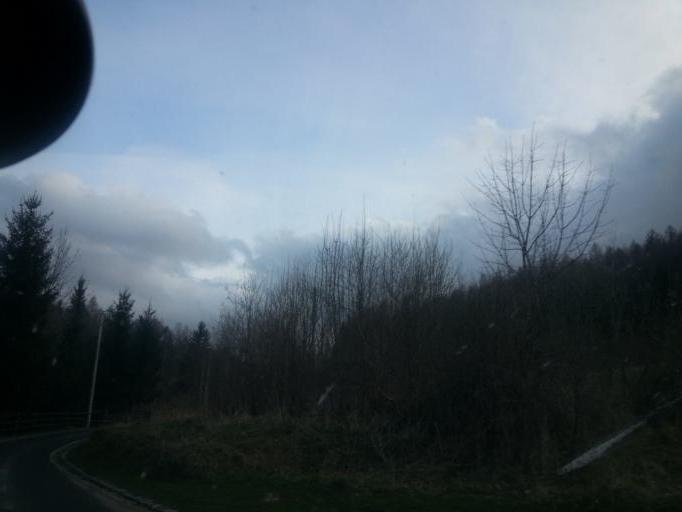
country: PL
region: Lower Silesian Voivodeship
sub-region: Powiat jeleniogorski
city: Podgorzyn
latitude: 50.8192
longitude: 15.6568
